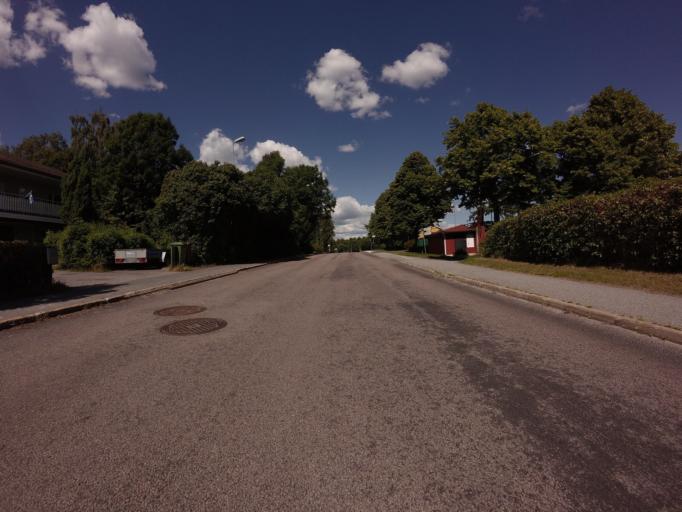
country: SE
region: Stockholm
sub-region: Sollentuna Kommun
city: Sollentuna
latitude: 59.4620
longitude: 17.9190
